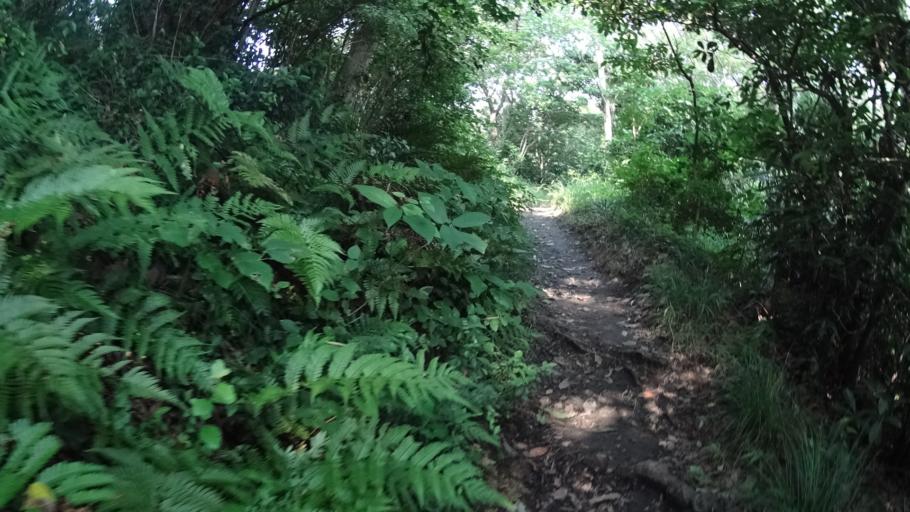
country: JP
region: Kanagawa
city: Zushi
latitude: 35.3032
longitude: 139.6167
